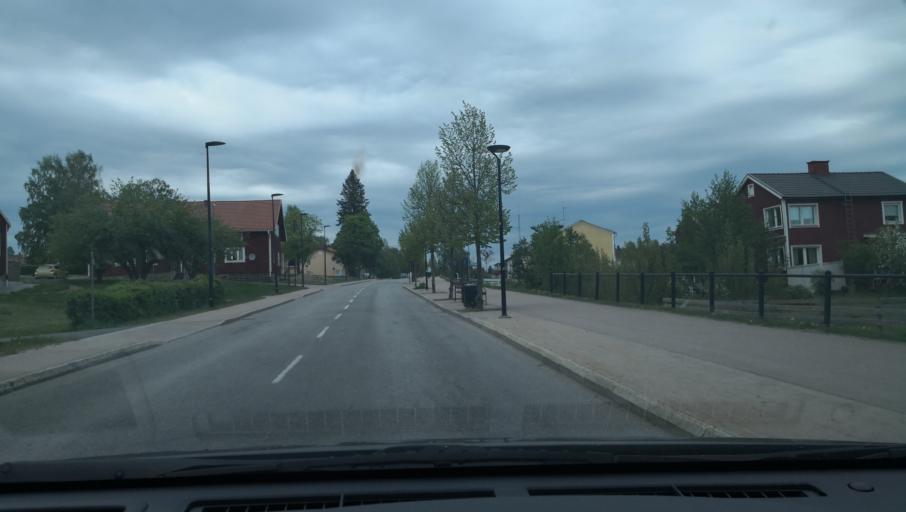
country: SE
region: Vaestmanland
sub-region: Skinnskattebergs Kommun
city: Skinnskatteberg
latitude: 59.8266
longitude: 15.6918
